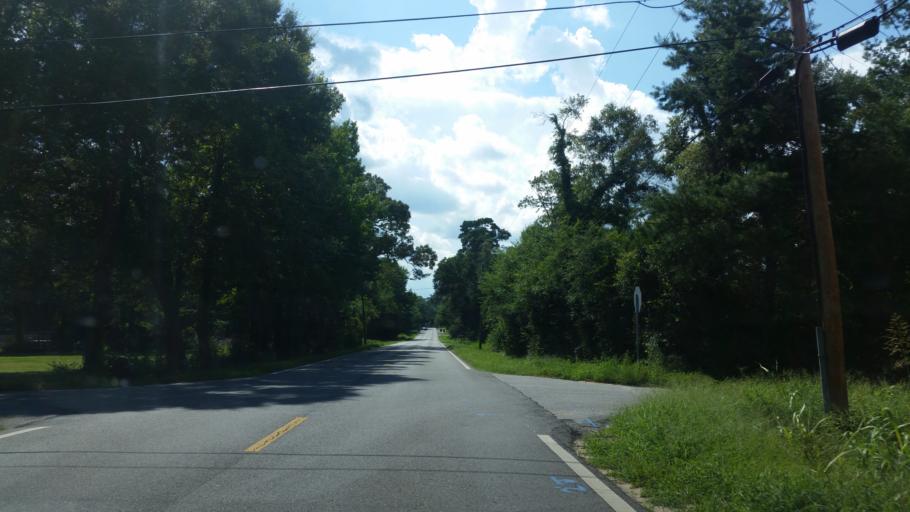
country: US
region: Florida
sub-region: Santa Rosa County
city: Pace
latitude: 30.5918
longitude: -87.1686
